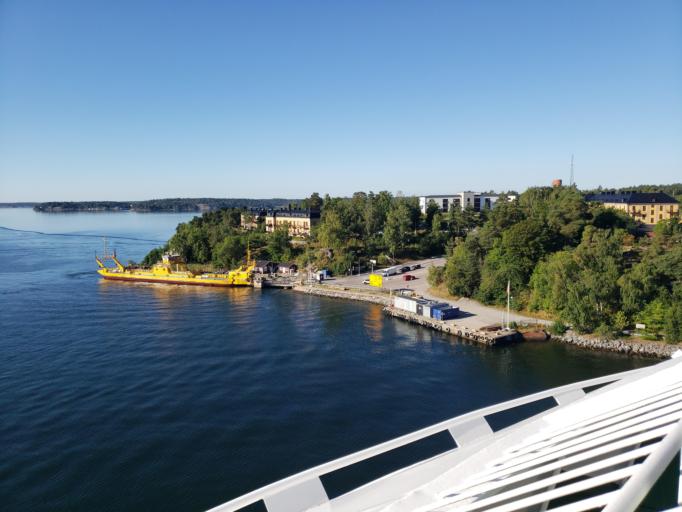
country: SE
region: Stockholm
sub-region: Varmdo Kommun
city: Mortnas
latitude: 59.3972
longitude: 18.4423
